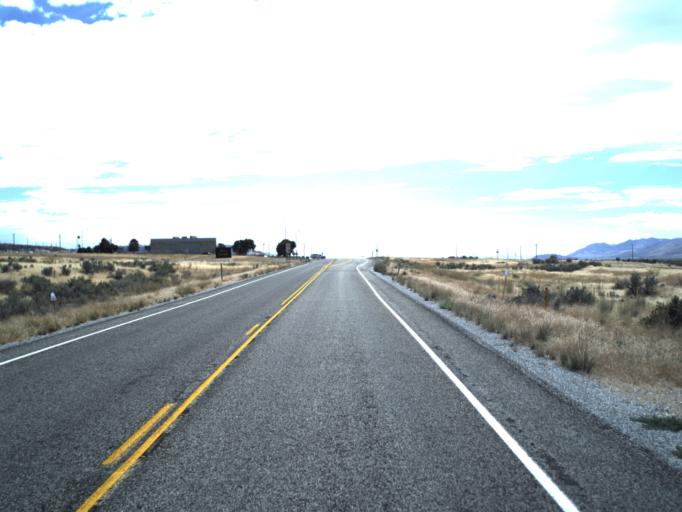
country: US
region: Utah
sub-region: Box Elder County
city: Tremonton
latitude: 41.6654
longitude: -112.4447
